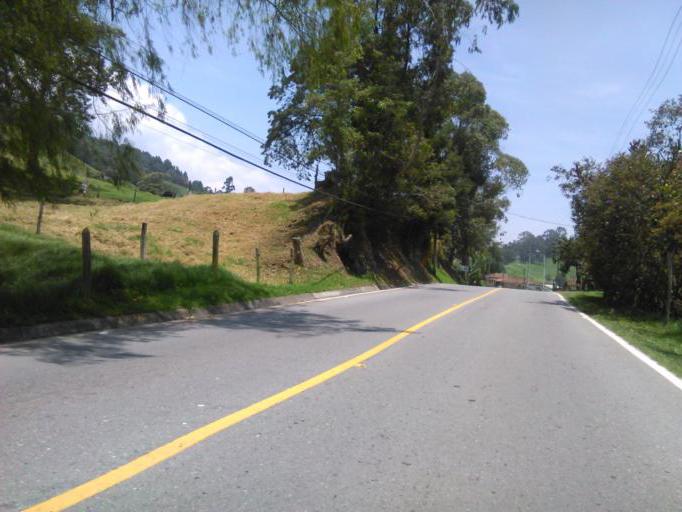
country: CO
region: Antioquia
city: La Union
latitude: 5.9943
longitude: -75.3779
